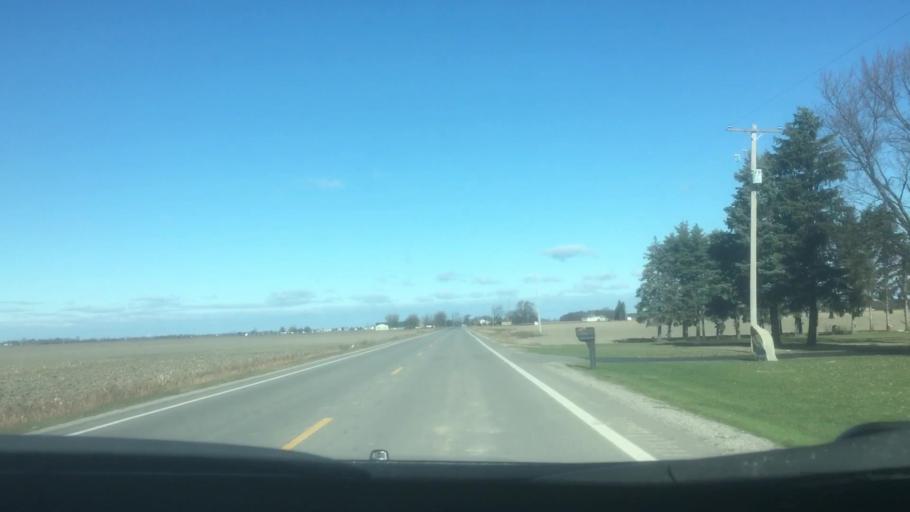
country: US
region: Michigan
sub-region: Tuscola County
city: Reese
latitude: 43.5304
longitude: -83.7588
